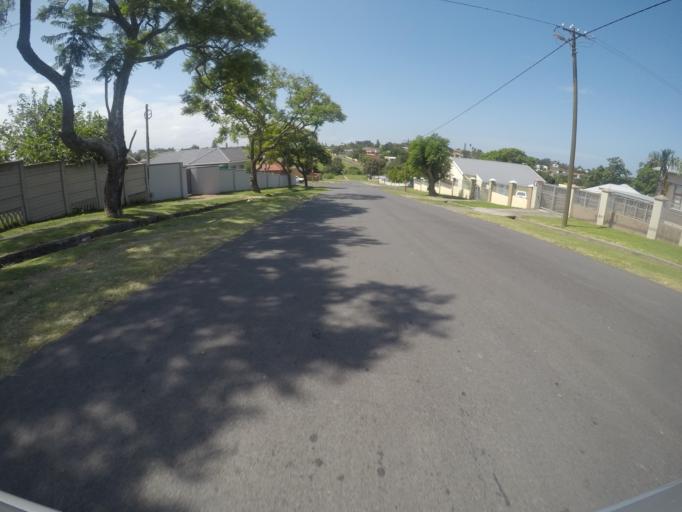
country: ZA
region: Eastern Cape
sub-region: Buffalo City Metropolitan Municipality
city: East London
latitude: -32.9785
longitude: 27.8756
